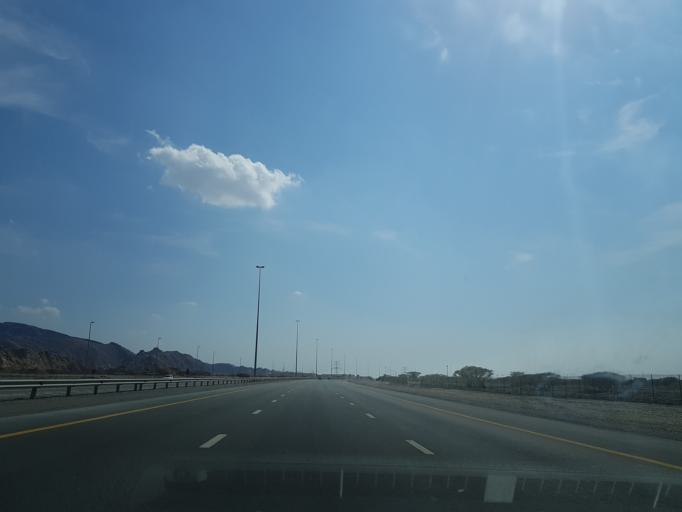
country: AE
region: Ra's al Khaymah
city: Ras al-Khaimah
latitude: 25.7838
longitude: 56.0312
